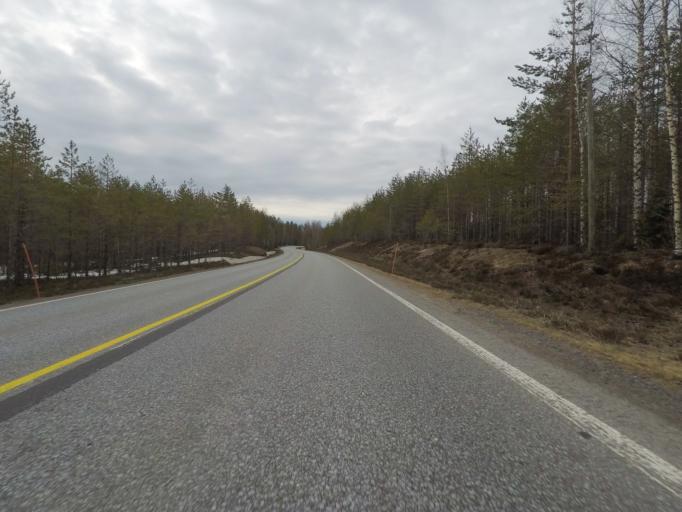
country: FI
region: Central Finland
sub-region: Jyvaeskylae
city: Toivakka
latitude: 62.1801
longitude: 26.1799
